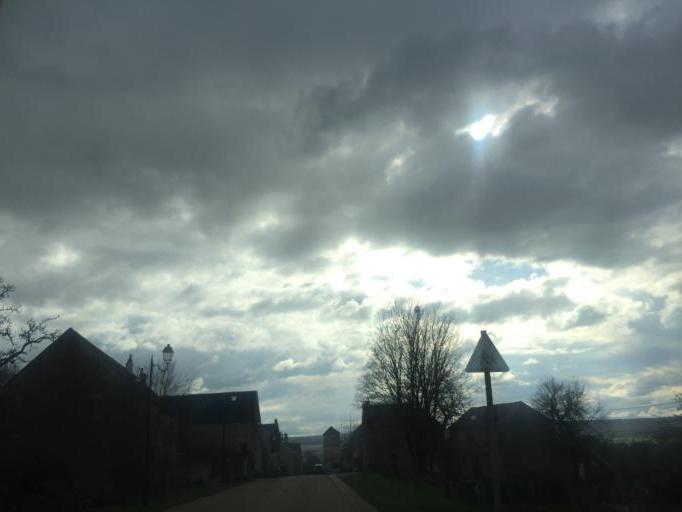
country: FR
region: Bourgogne
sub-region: Departement de l'Yonne
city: Avallon
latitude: 47.4677
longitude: 3.7941
